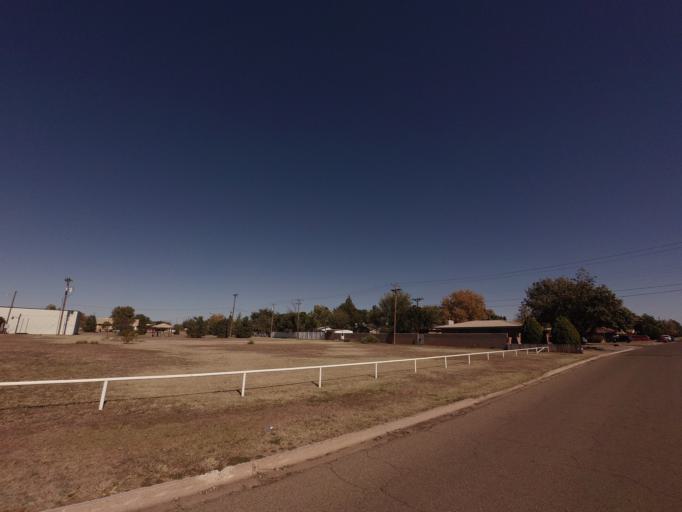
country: US
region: New Mexico
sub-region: Curry County
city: Clovis
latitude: 34.4239
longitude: -103.2057
